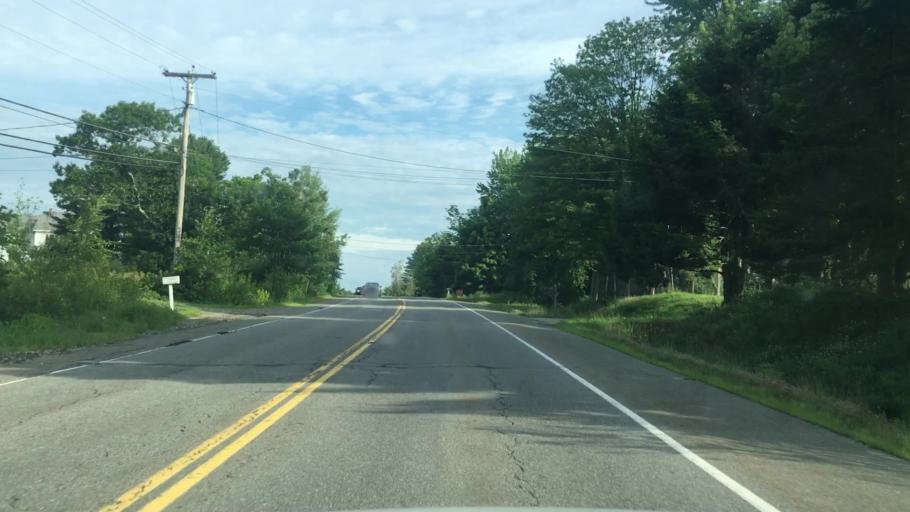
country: US
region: Maine
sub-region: Cumberland County
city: Gorham
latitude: 43.6452
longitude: -70.4223
